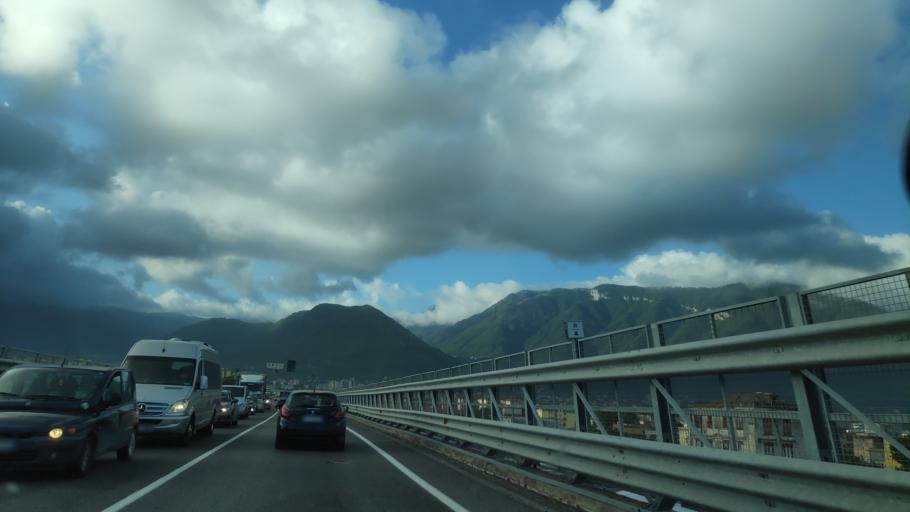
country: IT
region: Campania
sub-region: Provincia di Napoli
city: Castellammare di Stabia
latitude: 40.7166
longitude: 14.4947
